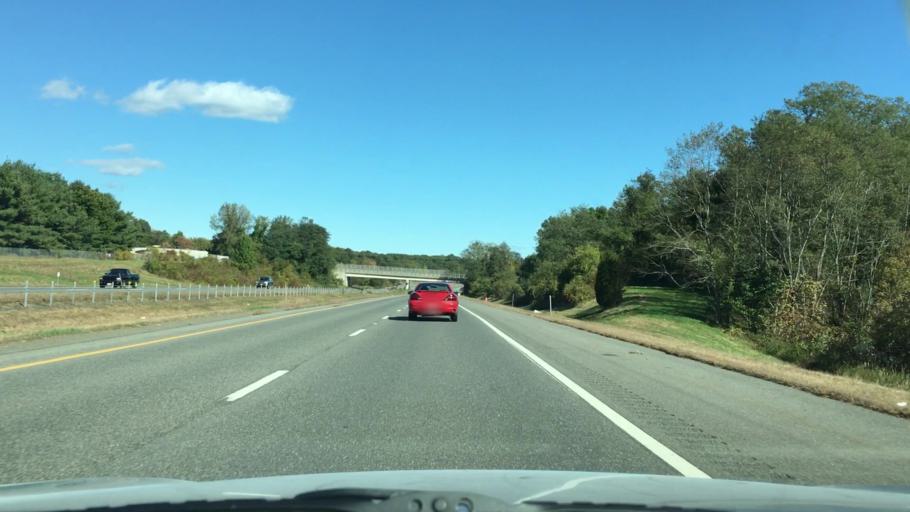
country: US
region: Massachusetts
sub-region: Hampden County
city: Agawam
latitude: 42.0605
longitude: -72.6604
